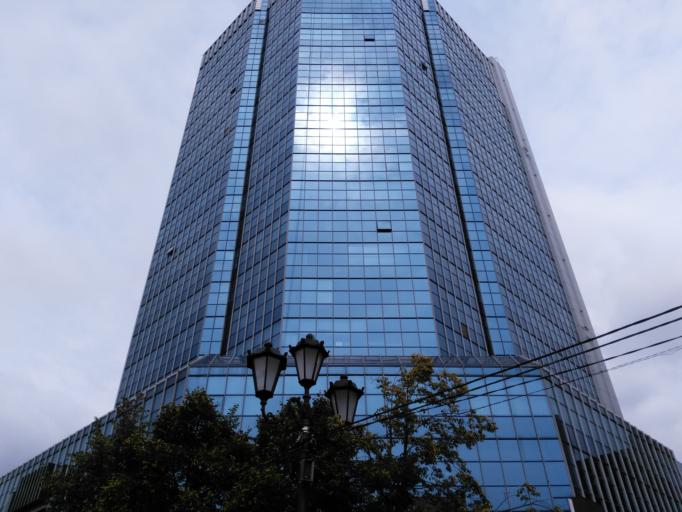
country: RU
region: Chelyabinsk
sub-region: Gorod Chelyabinsk
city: Chelyabinsk
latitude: 55.1643
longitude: 61.4008
